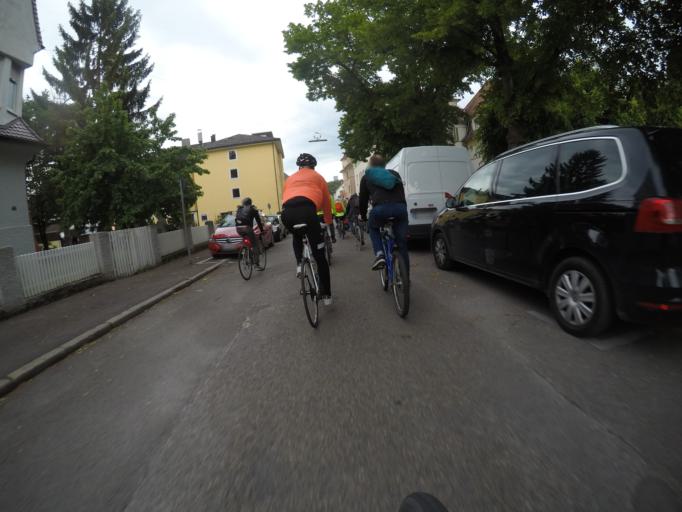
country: DE
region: Baden-Wuerttemberg
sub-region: Regierungsbezirk Stuttgart
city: Esslingen
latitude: 48.7339
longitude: 9.3260
